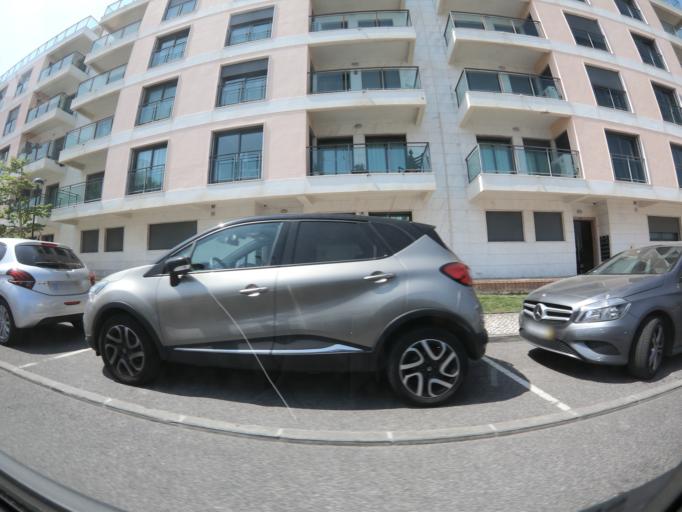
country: PT
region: Lisbon
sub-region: Oeiras
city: Oeiras
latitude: 38.7035
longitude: -9.3098
